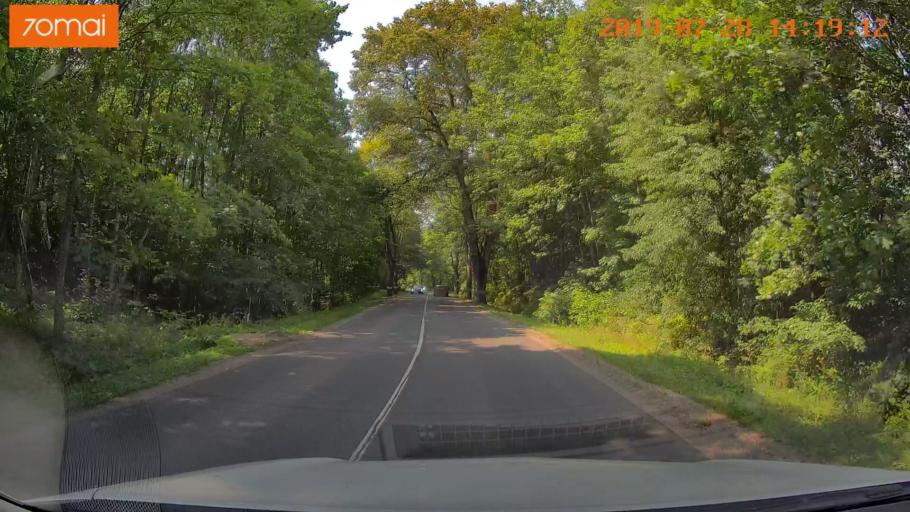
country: RU
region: Kaliningrad
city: Volochayevskoye
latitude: 54.8187
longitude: 20.2296
